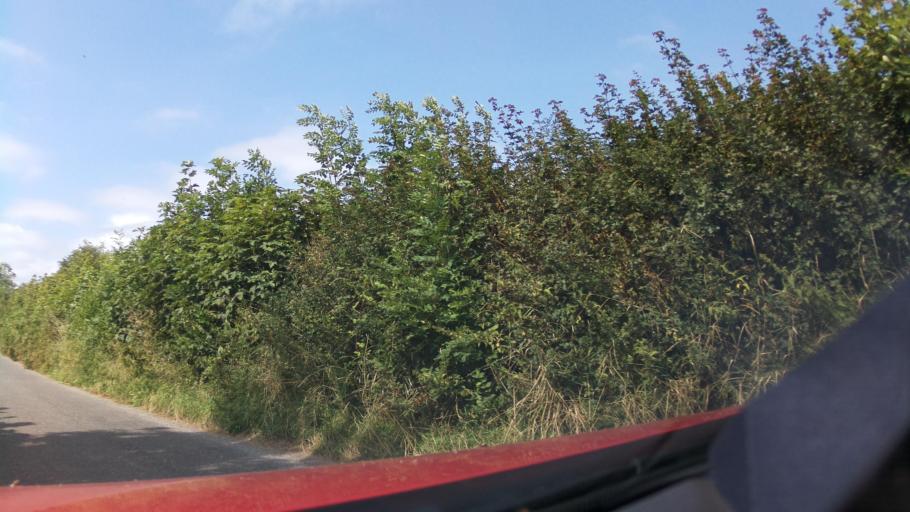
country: GB
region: England
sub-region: Borough of Torbay
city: Paignton
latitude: 50.4000
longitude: -3.6023
